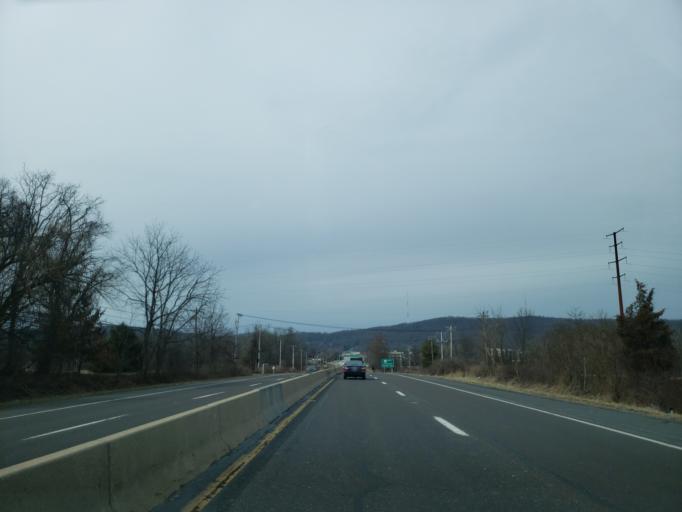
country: US
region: Pennsylvania
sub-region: Lehigh County
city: Coopersburg
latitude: 40.5452
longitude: -75.4202
